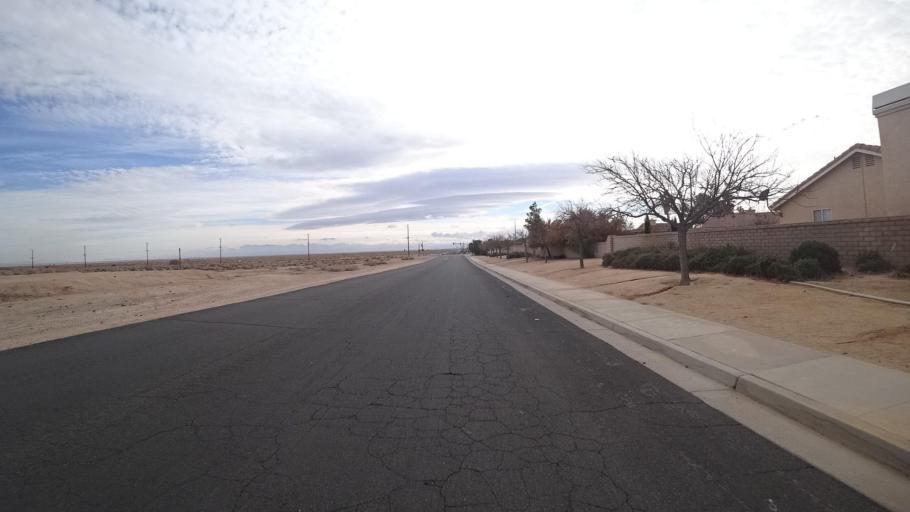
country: US
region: California
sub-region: Kern County
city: Rosamond
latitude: 34.8668
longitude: -118.1495
